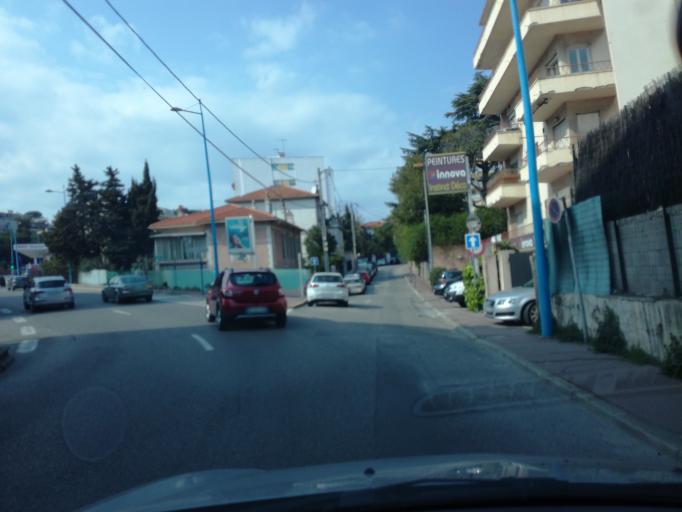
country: FR
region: Provence-Alpes-Cote d'Azur
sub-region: Departement des Alpes-Maritimes
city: Le Cannet
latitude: 43.5705
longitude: 7.0161
